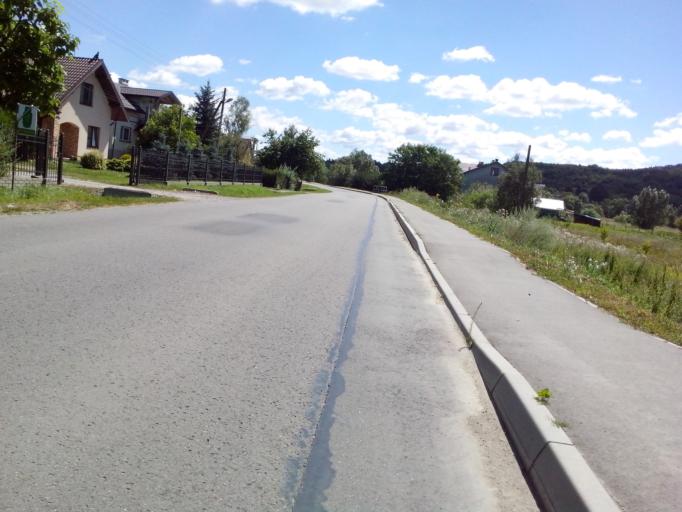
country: PL
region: Subcarpathian Voivodeship
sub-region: Powiat brzozowski
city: Domaradz
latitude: 49.7920
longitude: 21.9535
